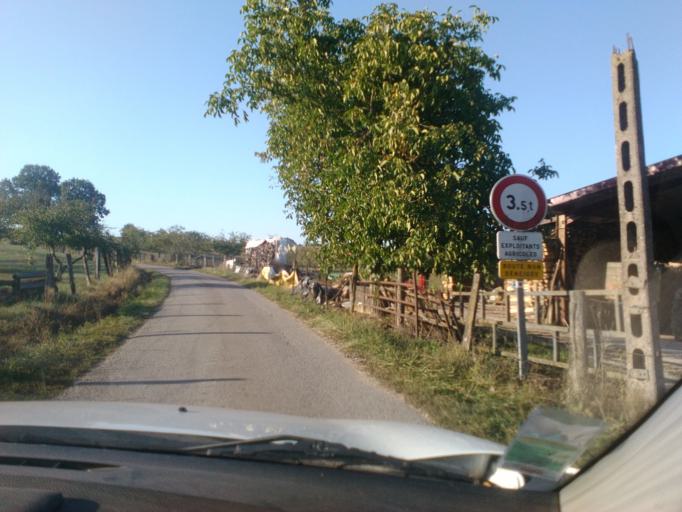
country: FR
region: Lorraine
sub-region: Departement des Vosges
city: Mirecourt
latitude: 48.2846
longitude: 6.1899
